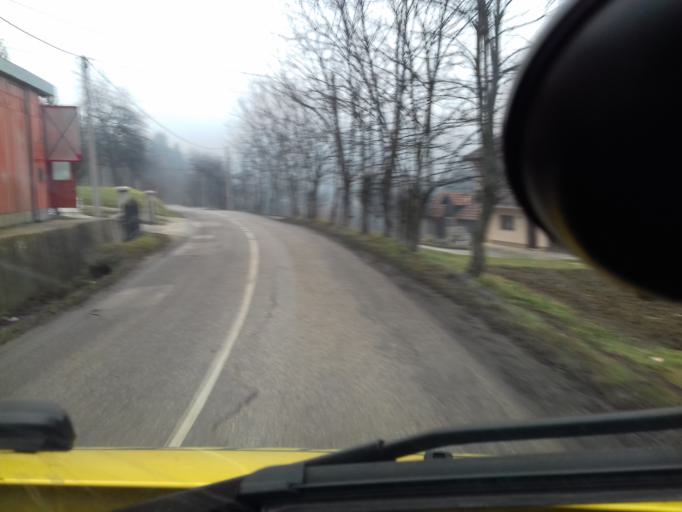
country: BA
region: Federation of Bosnia and Herzegovina
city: Lokvine
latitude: 44.1973
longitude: 17.8727
